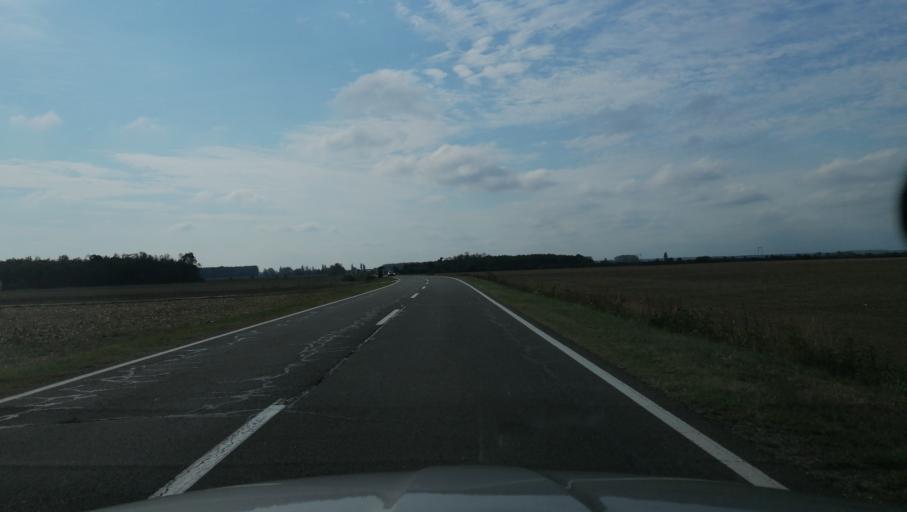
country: RS
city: Bosut
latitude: 44.9588
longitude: 19.3799
